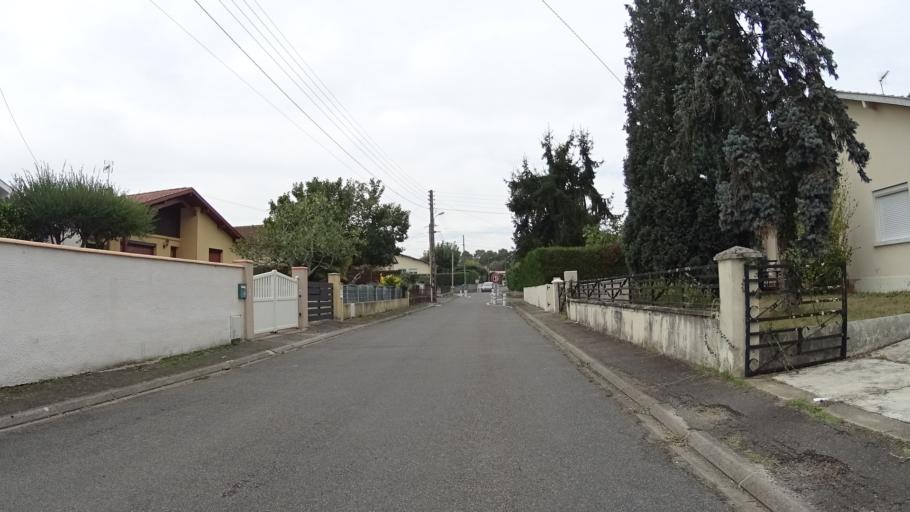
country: FR
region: Aquitaine
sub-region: Departement des Landes
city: Saint-Paul-les-Dax
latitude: 43.7303
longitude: -1.0755
